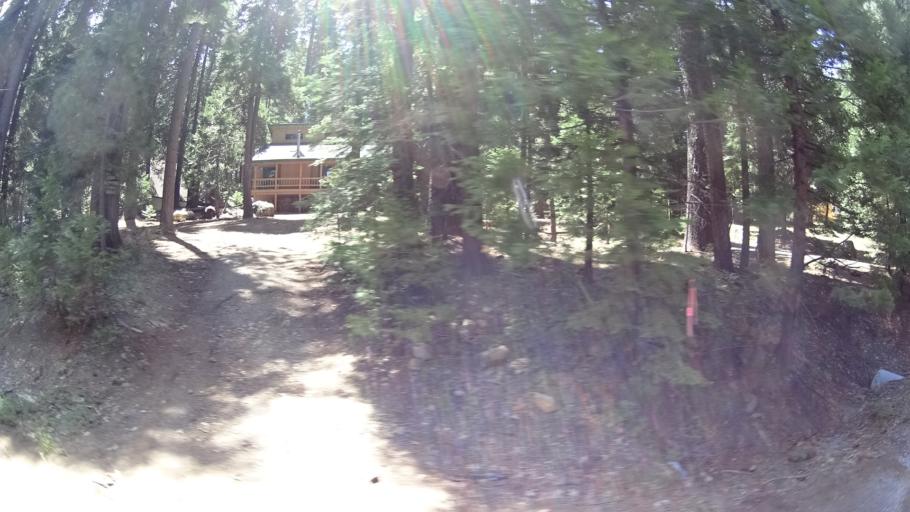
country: US
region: California
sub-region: Calaveras County
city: Arnold
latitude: 38.3040
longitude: -120.2564
